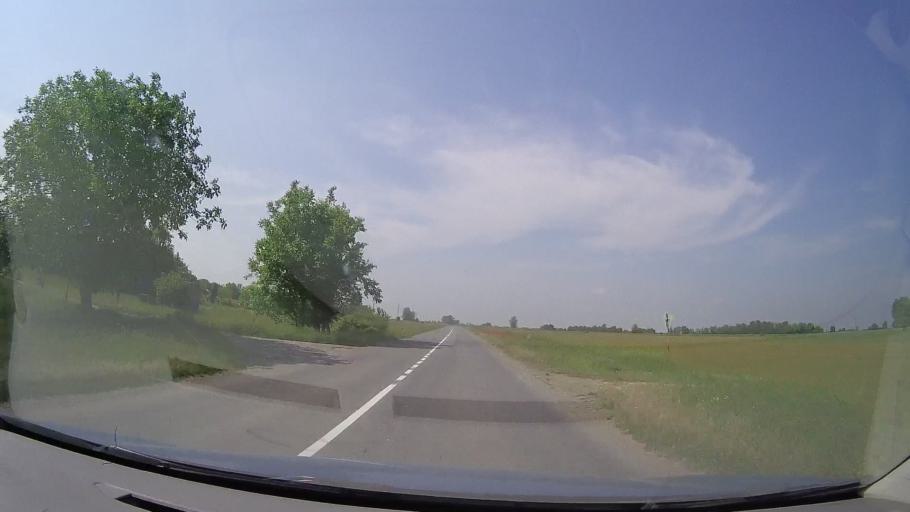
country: RS
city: Samos
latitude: 45.1953
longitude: 20.7695
